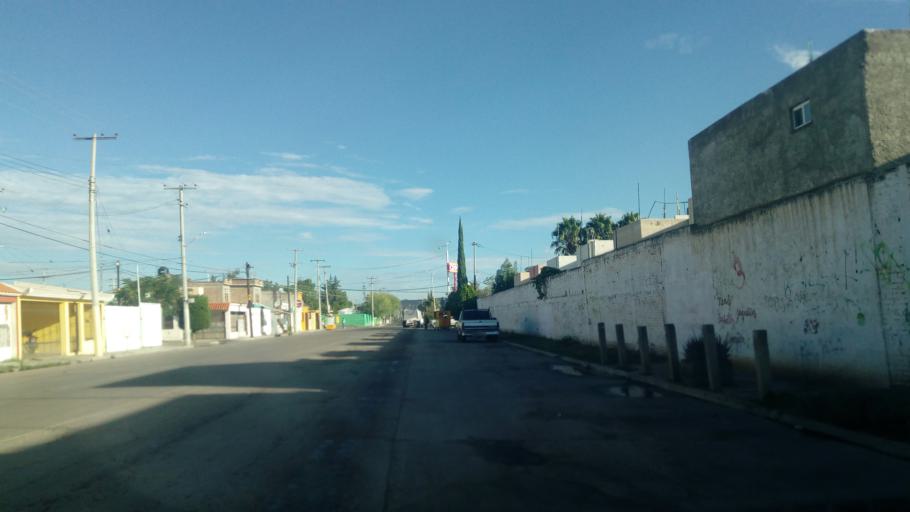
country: MX
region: Durango
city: Victoria de Durango
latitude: 24.0518
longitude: -104.6066
